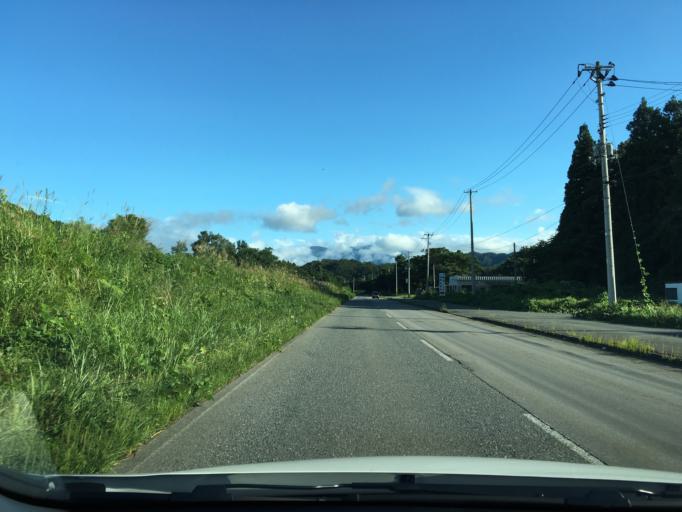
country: JP
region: Yamagata
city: Yonezawa
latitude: 37.9185
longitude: 140.1597
